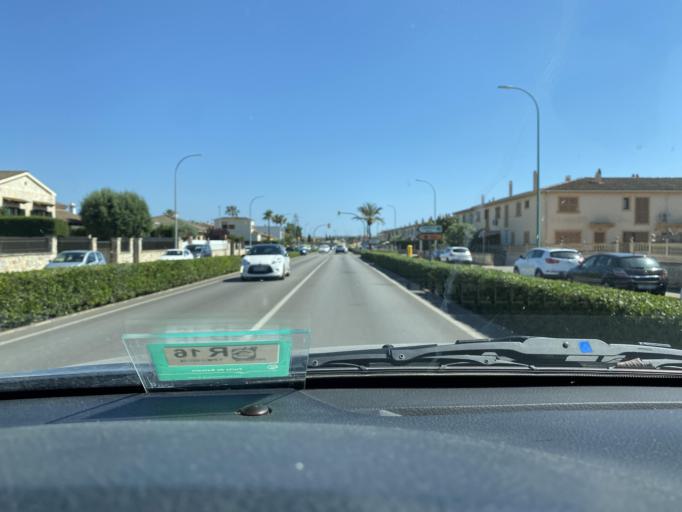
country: ES
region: Balearic Islands
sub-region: Illes Balears
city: Palma
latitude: 39.6108
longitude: 2.6847
